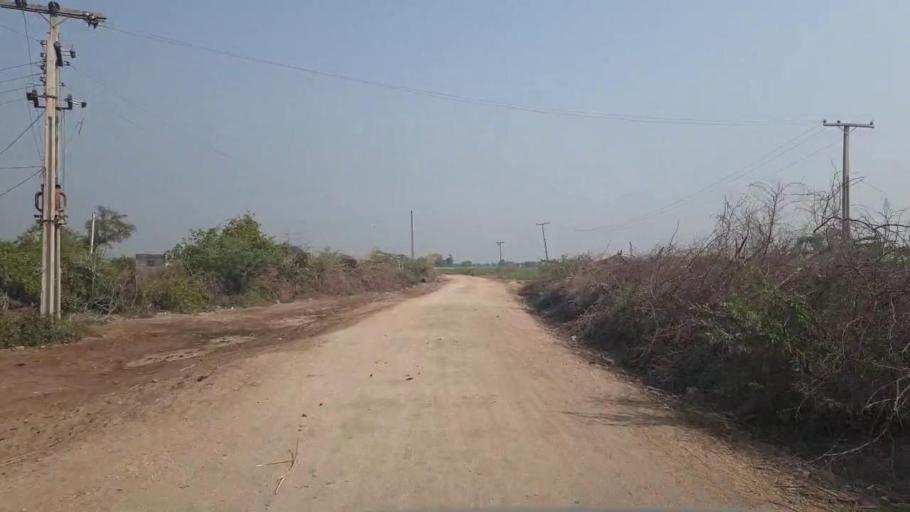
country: PK
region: Sindh
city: Umarkot
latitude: 25.3987
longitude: 69.6985
